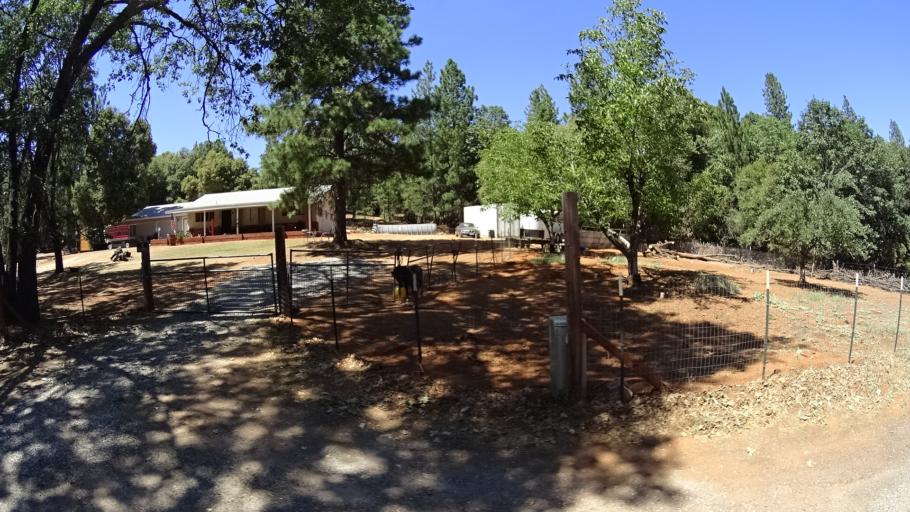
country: US
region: California
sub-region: Calaveras County
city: Mountain Ranch
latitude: 38.2841
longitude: -120.5097
